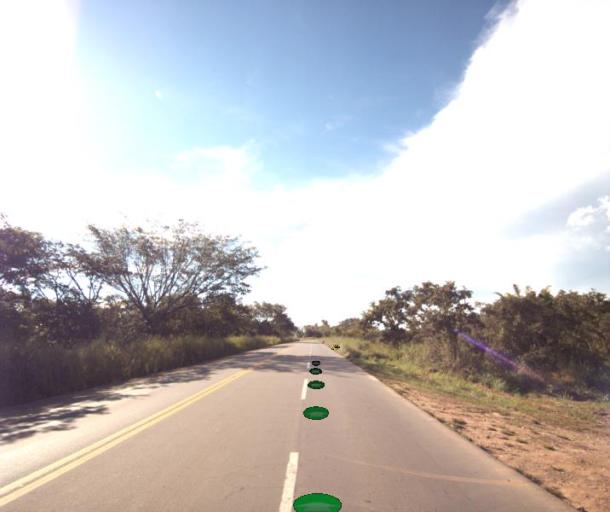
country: BR
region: Goias
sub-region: Rialma
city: Rialma
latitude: -15.4302
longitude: -49.5123
